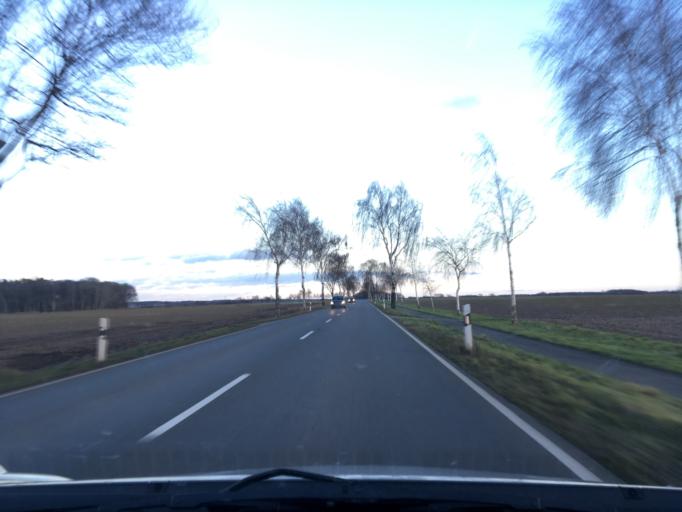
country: DE
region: Lower Saxony
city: Ratzlingen
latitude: 52.9753
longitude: 10.6318
